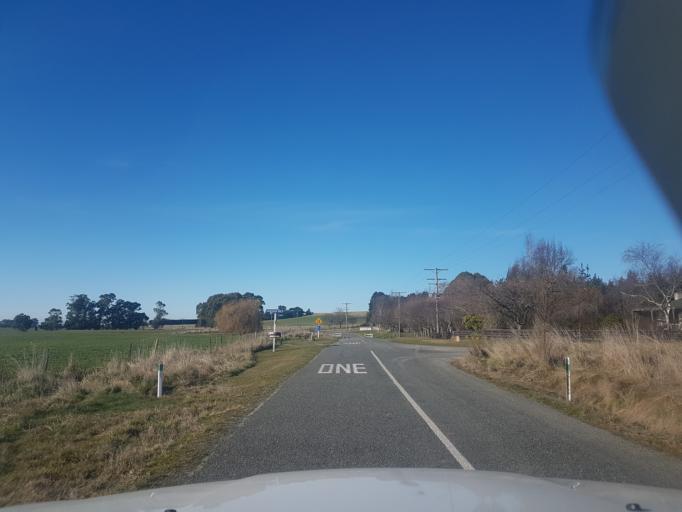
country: NZ
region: Canterbury
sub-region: Timaru District
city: Pleasant Point
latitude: -44.2882
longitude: 171.0793
